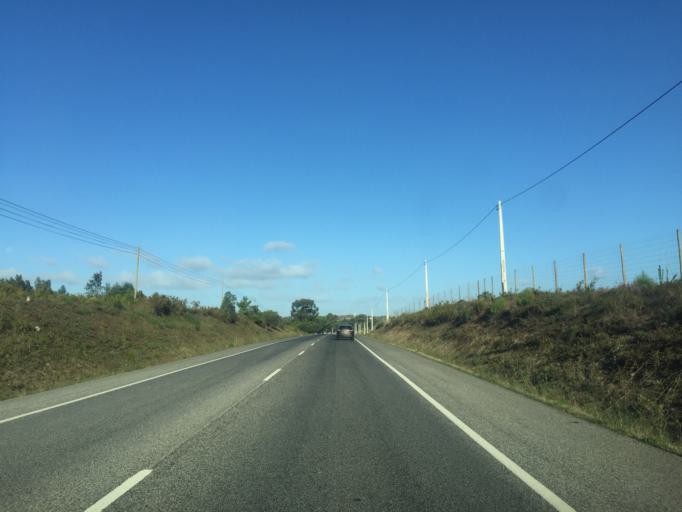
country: PT
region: Lisbon
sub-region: Azambuja
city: Alcoentre
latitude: 39.1895
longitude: -8.9476
